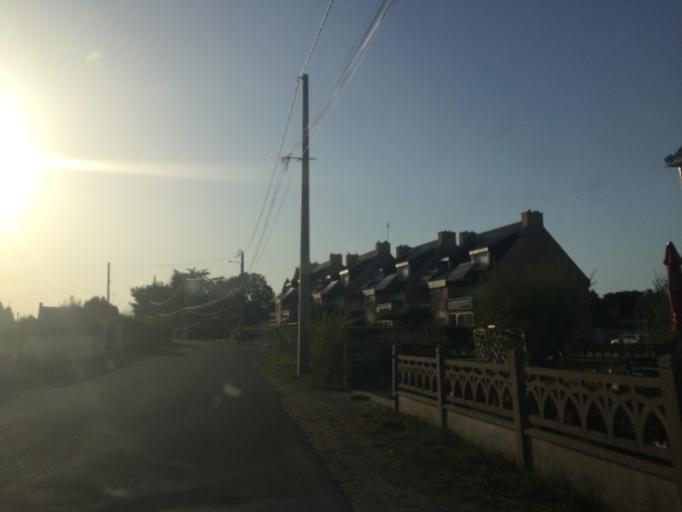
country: FR
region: Brittany
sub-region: Departement du Morbihan
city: Damgan
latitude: 47.5170
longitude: -2.5507
